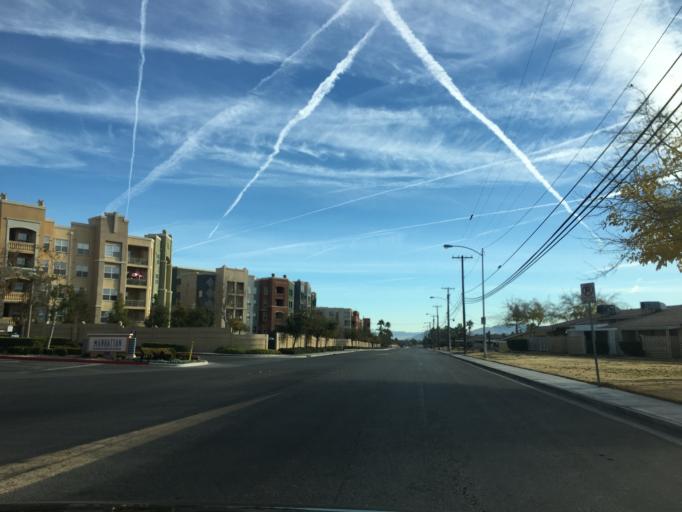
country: US
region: Nevada
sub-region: Clark County
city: Enterprise
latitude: 36.0210
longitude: -115.1717
